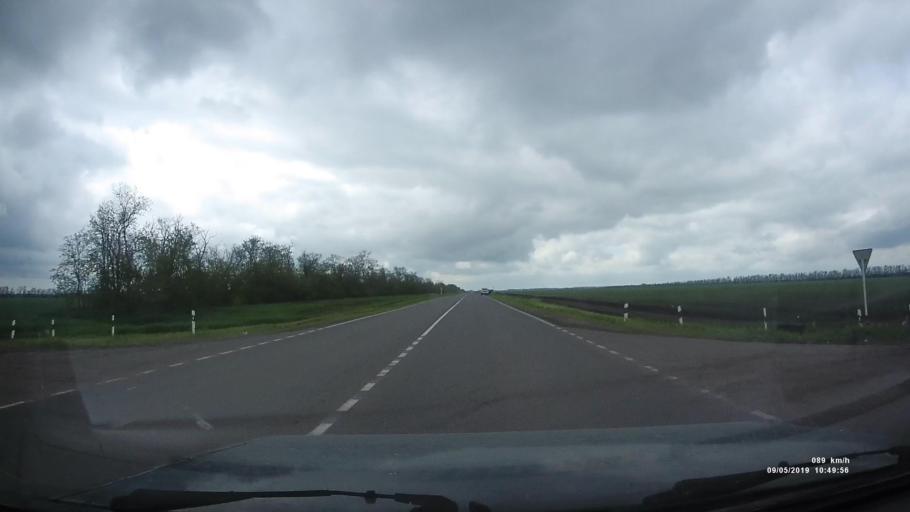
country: RU
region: Rostov
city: Peshkovo
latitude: 46.9360
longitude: 39.3554
